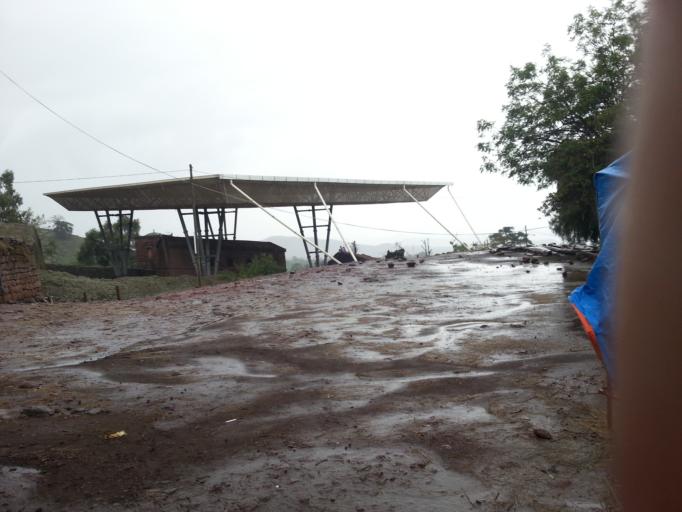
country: ET
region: Amhara
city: Lalibela
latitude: 12.0341
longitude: 39.0435
